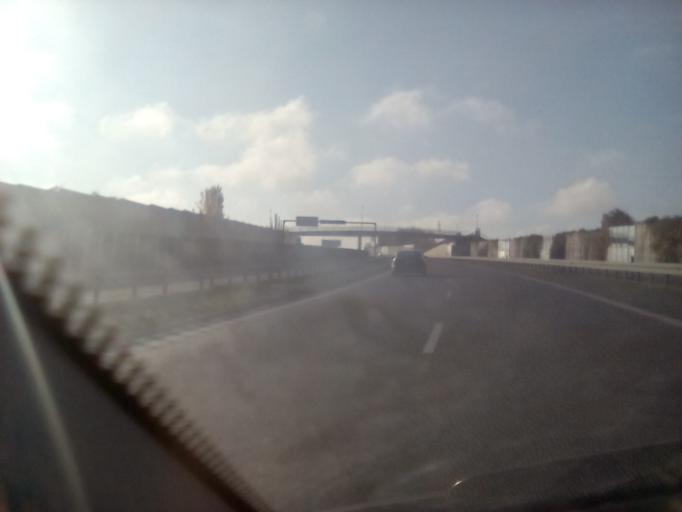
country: PL
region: Masovian Voivodeship
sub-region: Powiat grojecki
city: Grojec
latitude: 51.8663
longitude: 20.8506
